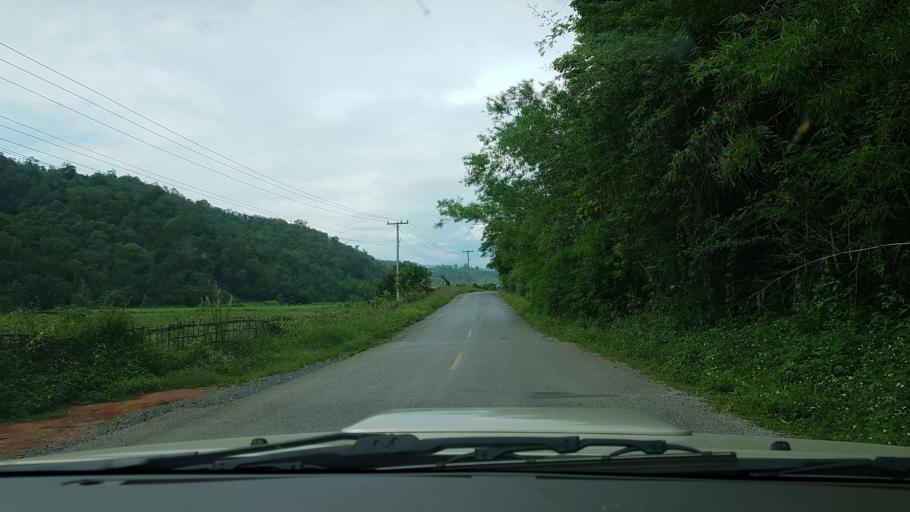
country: LA
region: Loungnamtha
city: Muang Nale
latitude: 20.3933
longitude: 101.7513
